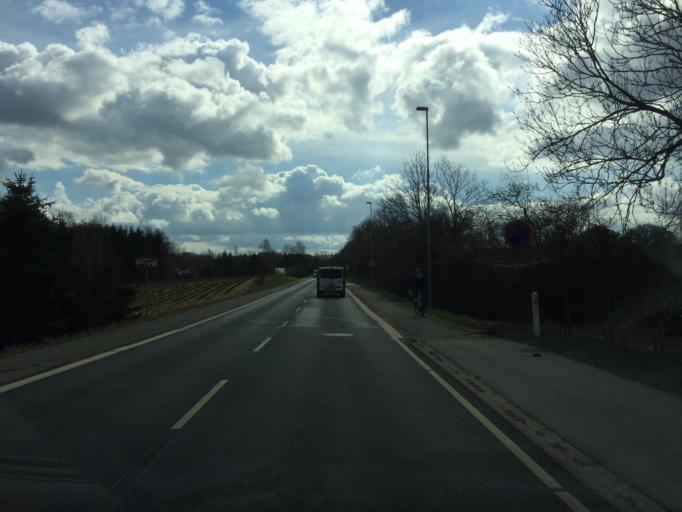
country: DK
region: South Denmark
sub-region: Nordfyns Kommune
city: Sonderso
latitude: 55.4020
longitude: 10.2607
